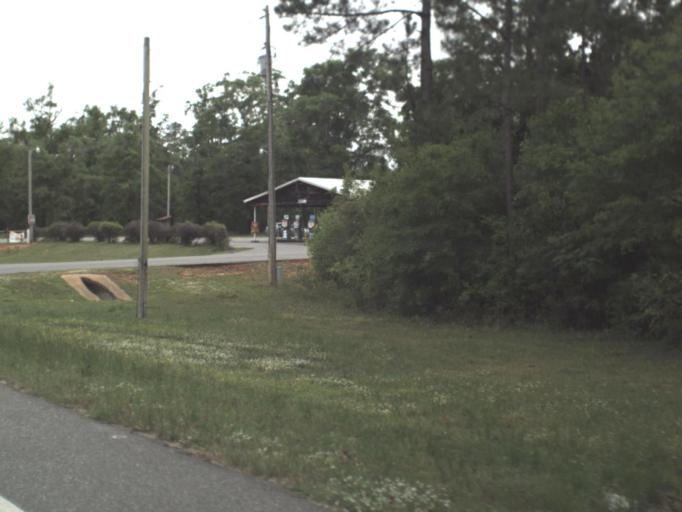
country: US
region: Florida
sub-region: Santa Rosa County
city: Point Baker
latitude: 30.7939
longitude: -87.0414
